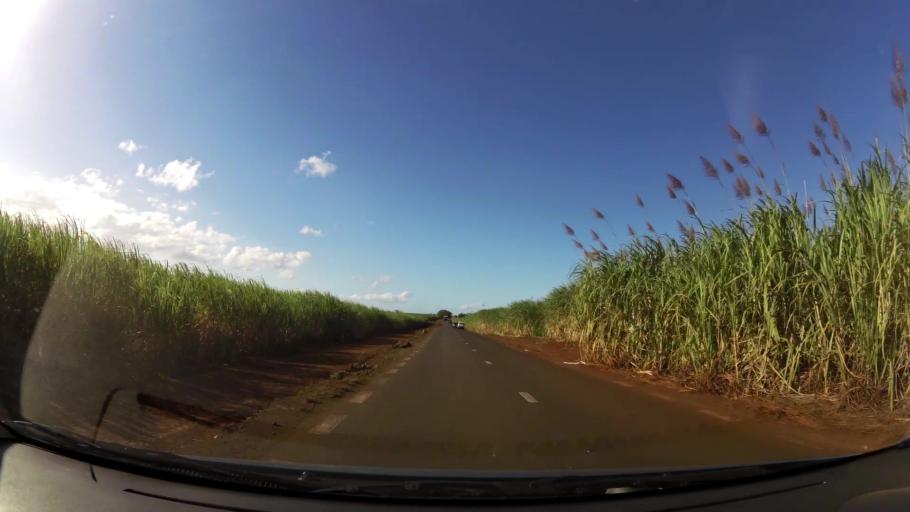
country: MU
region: Black River
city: Gros Cailloux
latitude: -20.2019
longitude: 57.4349
